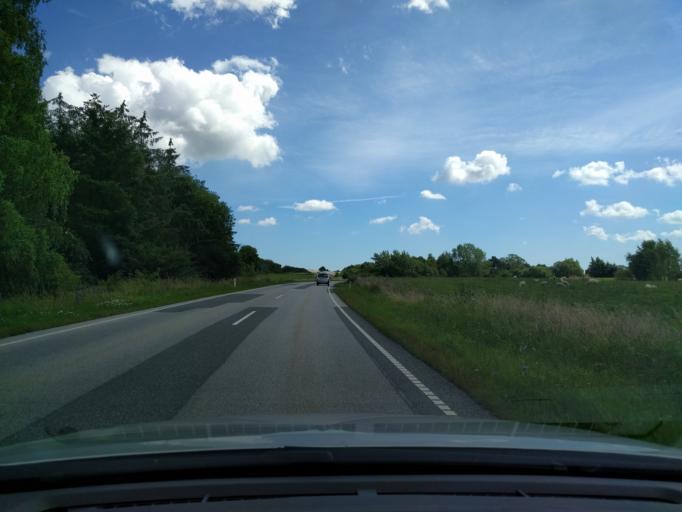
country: DK
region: Zealand
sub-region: Guldborgsund Kommune
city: Stubbekobing
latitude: 54.9202
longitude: 12.0372
